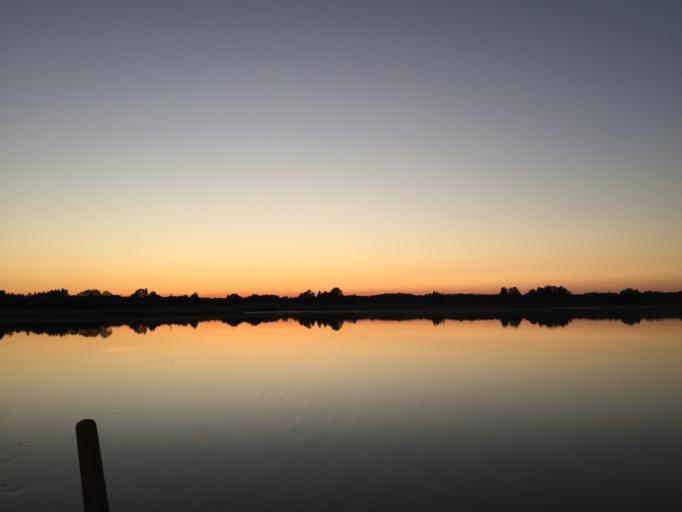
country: LV
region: Rezekne
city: Rezekne
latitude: 56.3698
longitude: 27.4147
